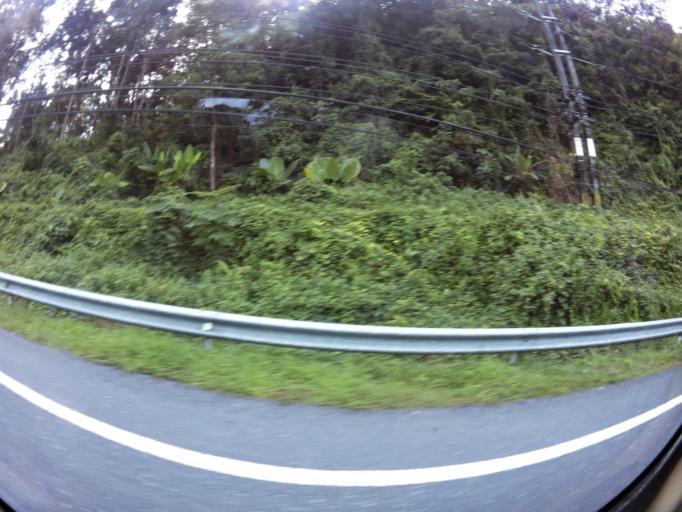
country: TH
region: Phuket
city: Patong
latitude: 7.9372
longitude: 98.2775
